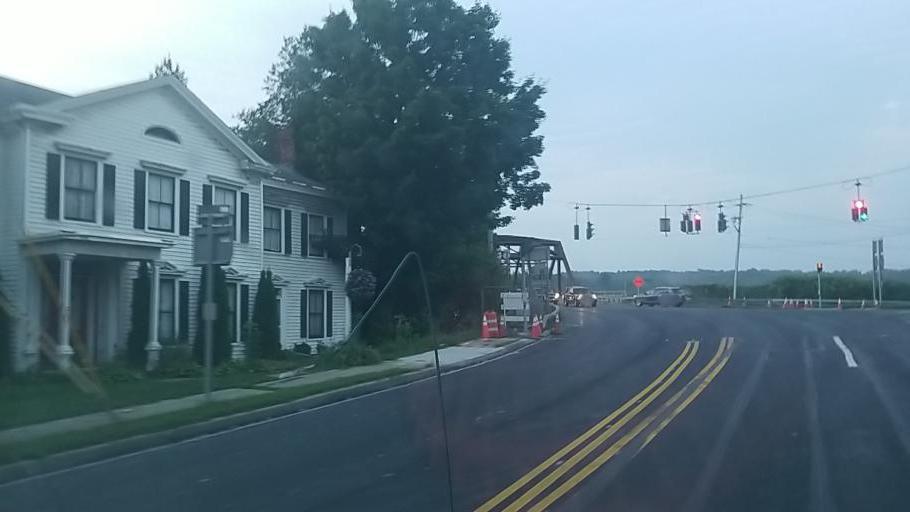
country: US
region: New York
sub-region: Montgomery County
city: Fonda
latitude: 42.9491
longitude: -74.3694
